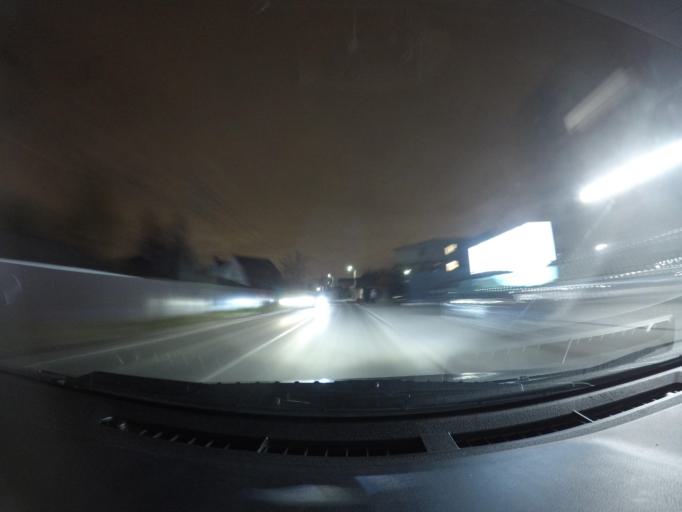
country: RU
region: Moskovskaya
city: Alekseyevka
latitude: 55.6058
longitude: 37.7915
